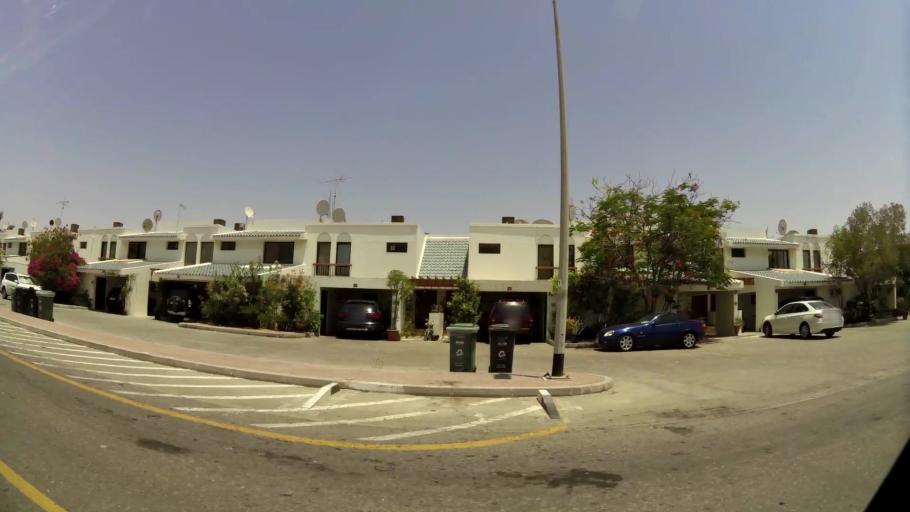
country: AE
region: Dubai
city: Dubai
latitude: 25.2038
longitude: 55.2475
